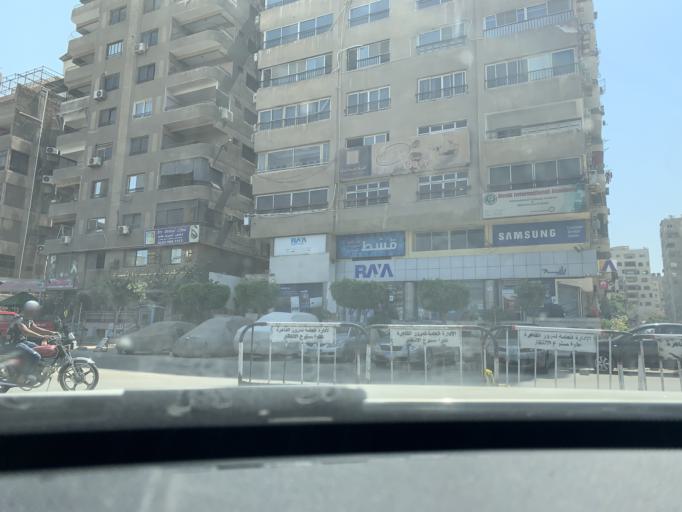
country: EG
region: Muhafazat al Qahirah
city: Cairo
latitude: 30.0490
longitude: 31.3470
